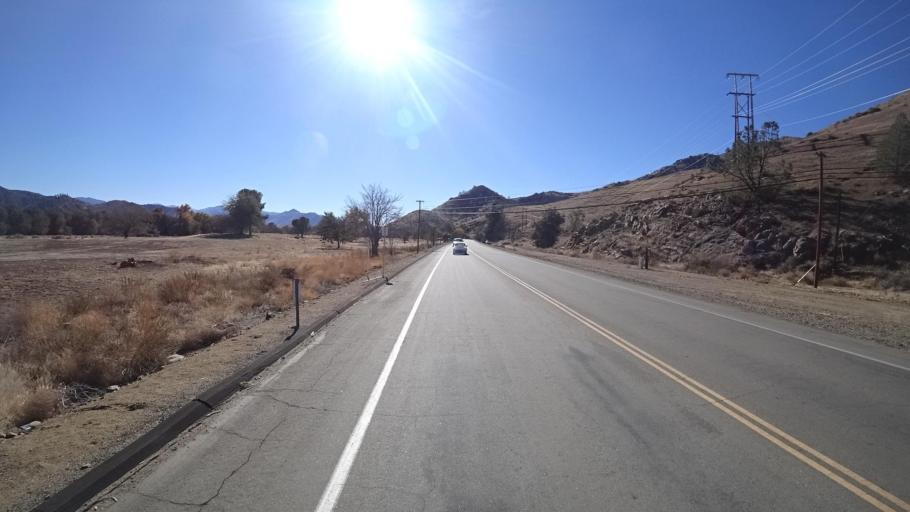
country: US
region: California
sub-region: Kern County
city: Kernville
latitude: 35.7427
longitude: -118.4242
